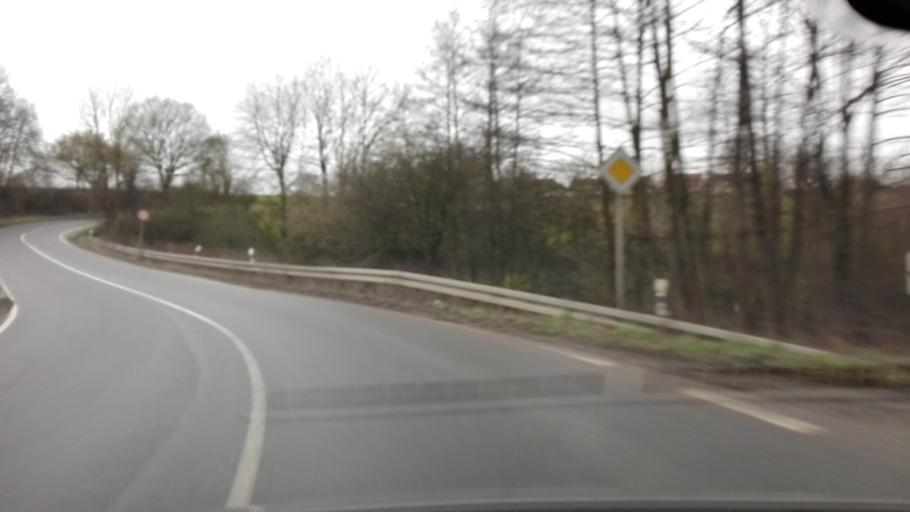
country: DE
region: North Rhine-Westphalia
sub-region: Regierungsbezirk Arnsberg
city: Frondenberg
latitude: 51.4812
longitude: 7.7354
